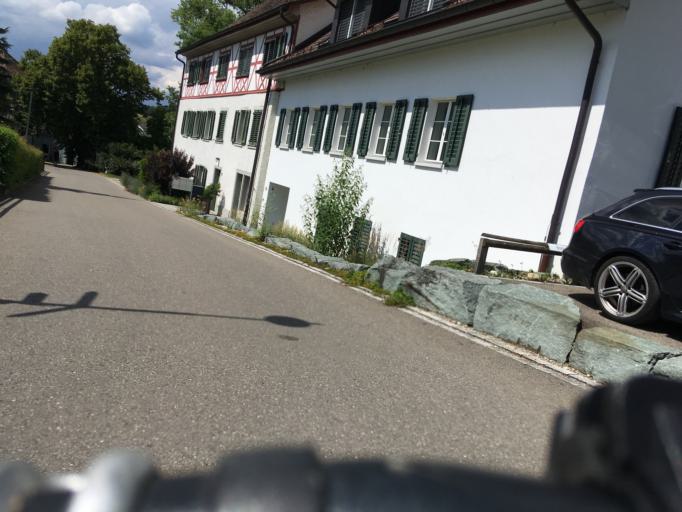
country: DE
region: Baden-Wuerttemberg
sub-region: Freiburg Region
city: Busingen
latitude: 47.6848
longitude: 8.6757
